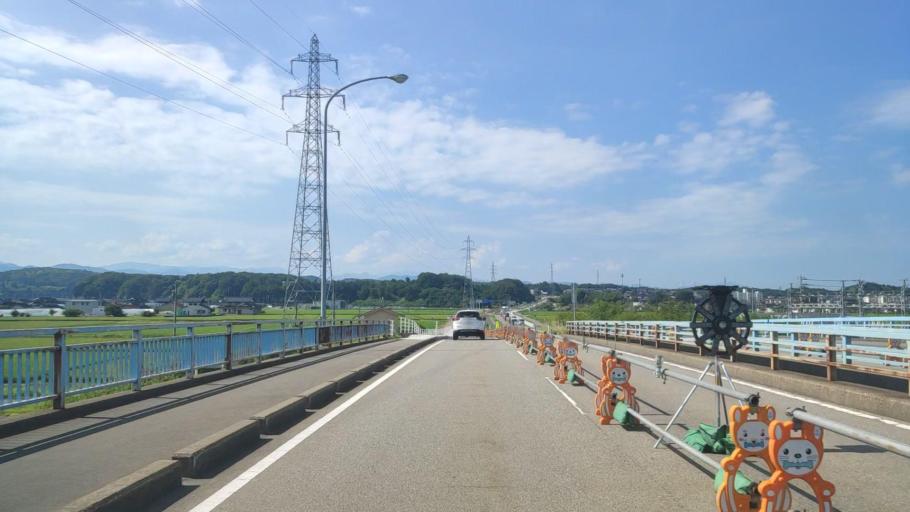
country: JP
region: Ishikawa
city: Komatsu
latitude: 36.4058
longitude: 136.5079
